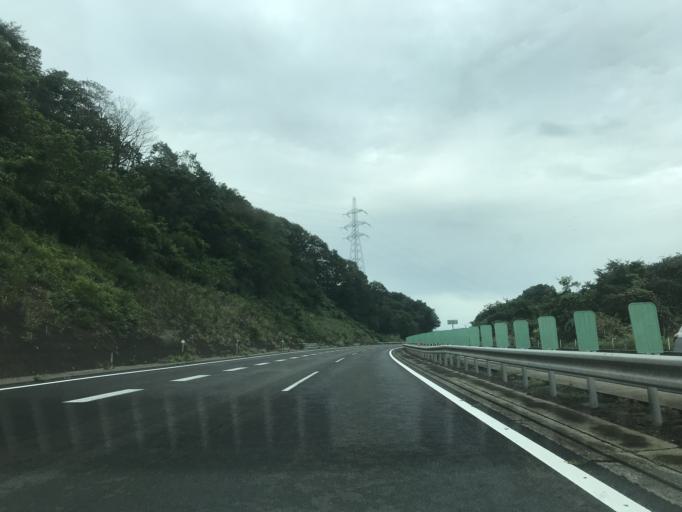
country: JP
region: Miyagi
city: Sendai
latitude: 38.2761
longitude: 140.8097
